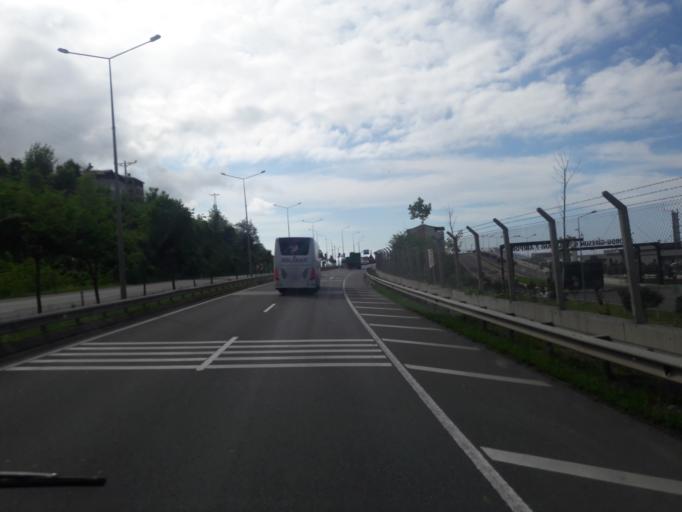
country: TR
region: Ordu
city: Gulyali
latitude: 40.9633
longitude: 38.0778
